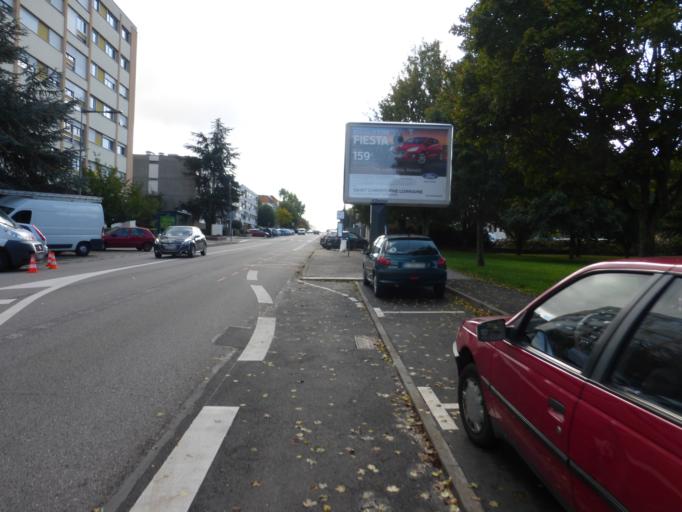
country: FR
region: Lorraine
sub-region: Departement de Meurthe-et-Moselle
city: Villers-les-Nancy
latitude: 48.6768
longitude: 6.1569
